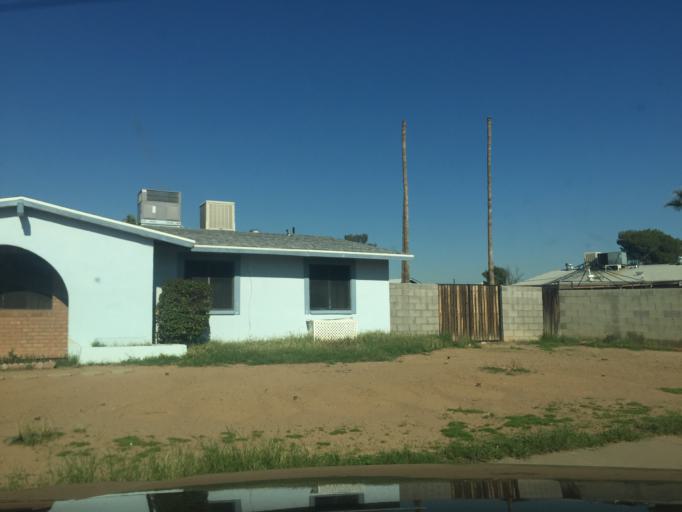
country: US
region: Arizona
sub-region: Maricopa County
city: Tolleson
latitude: 33.4764
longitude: -112.2143
